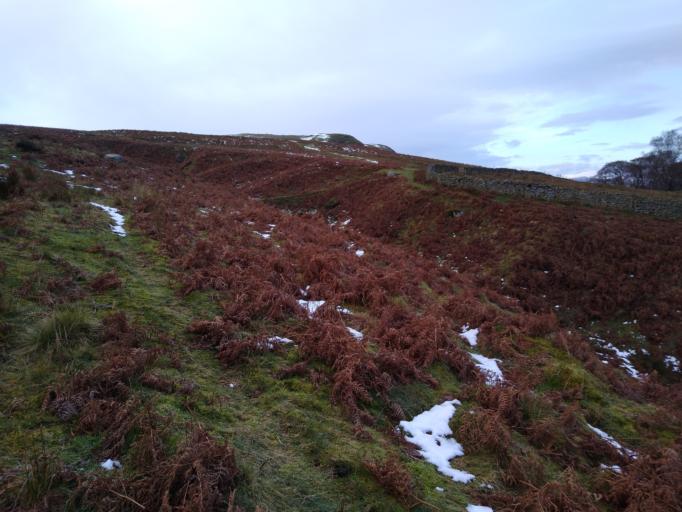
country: GB
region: England
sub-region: Cumbria
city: Penrith
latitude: 54.5910
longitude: -2.8162
